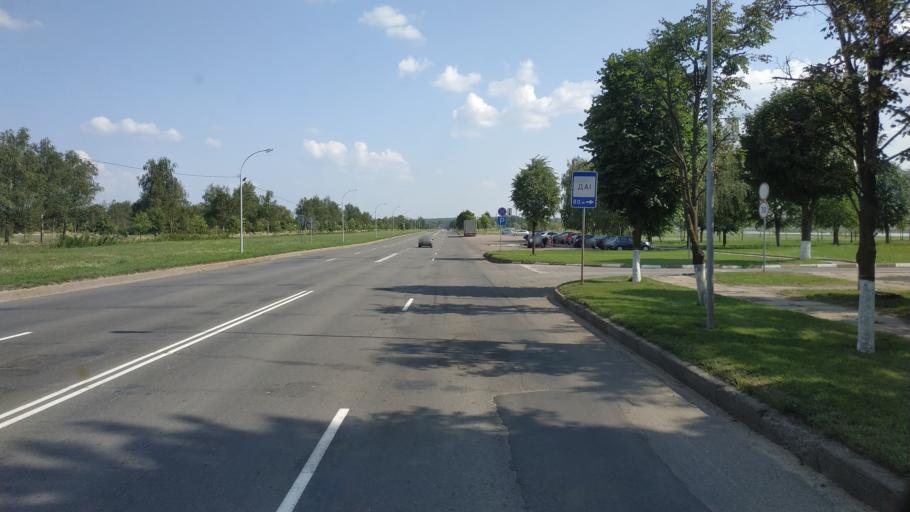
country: BY
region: Mogilev
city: Buynichy
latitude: 53.8647
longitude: 30.3180
